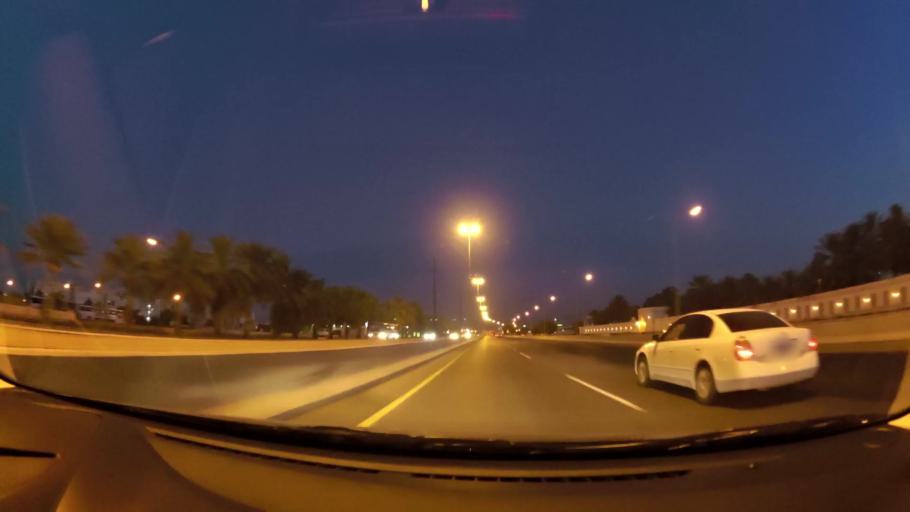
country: OM
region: Muhafazat Masqat
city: As Sib al Jadidah
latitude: 23.6209
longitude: 58.2401
